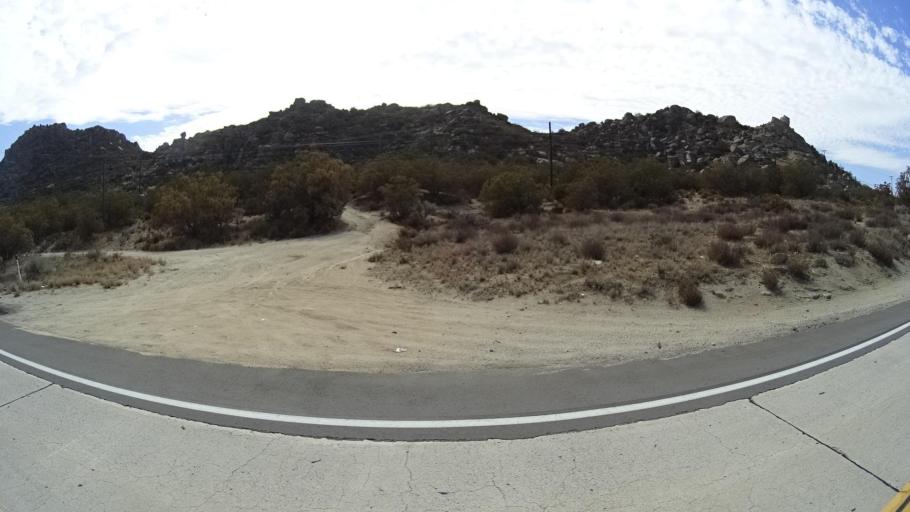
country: MX
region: Baja California
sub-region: Tecate
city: Cereso del Hongo
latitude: 32.6571
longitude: -116.2482
